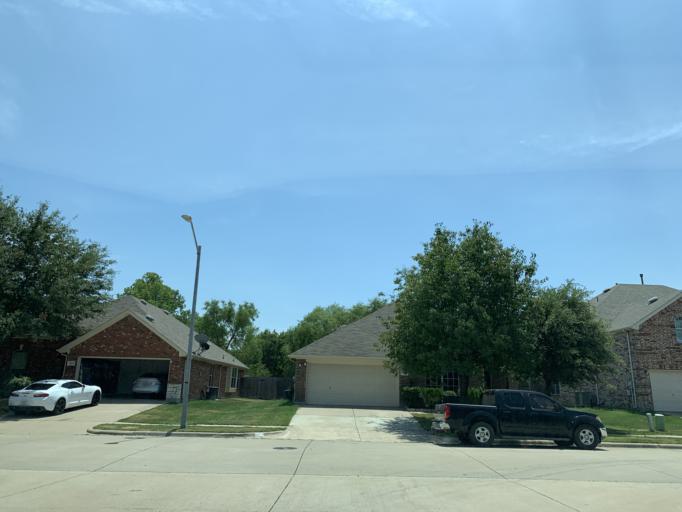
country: US
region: Texas
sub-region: Dallas County
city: Cedar Hill
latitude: 32.6441
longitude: -97.0227
